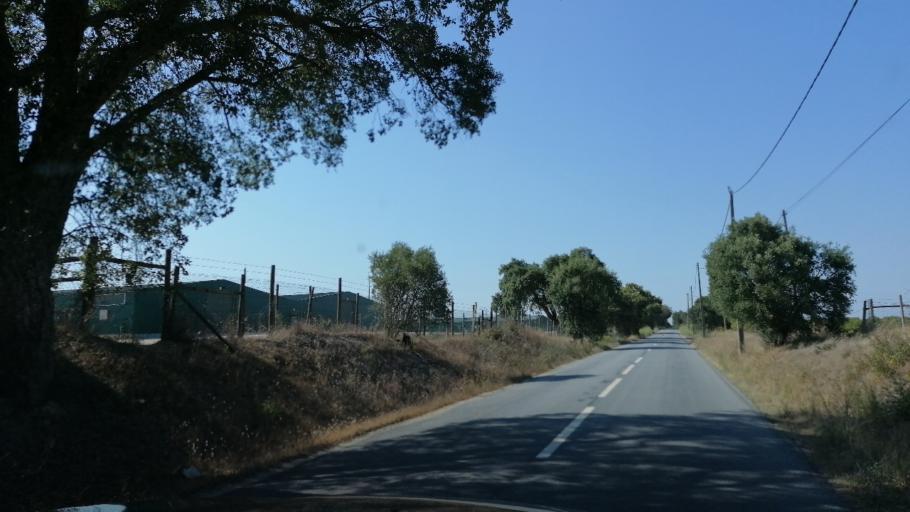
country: PT
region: Evora
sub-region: Vendas Novas
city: Vendas Novas
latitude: 38.7188
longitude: -8.6186
